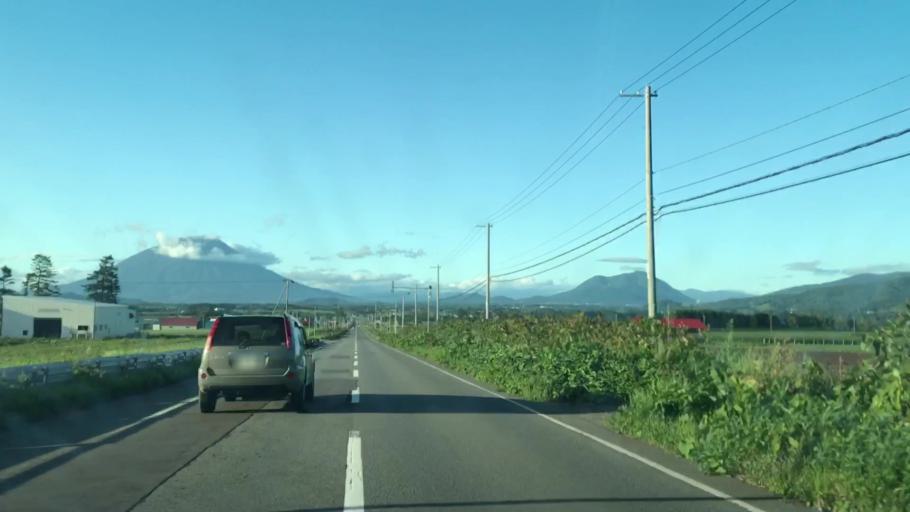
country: JP
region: Hokkaido
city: Date
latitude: 42.6295
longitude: 140.7999
